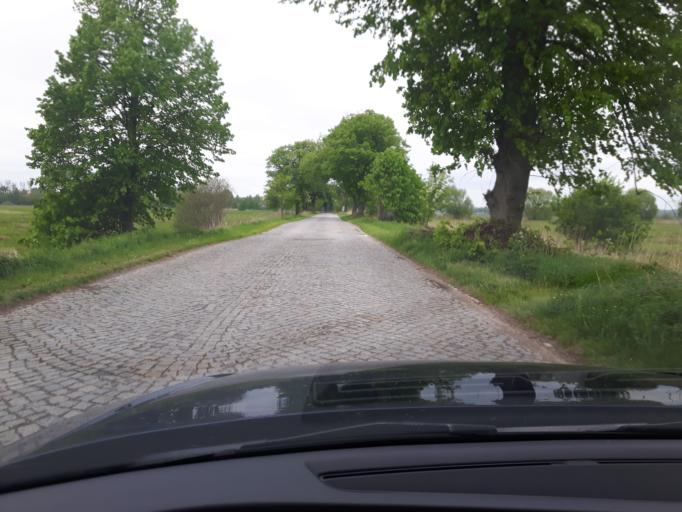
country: DE
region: Mecklenburg-Vorpommern
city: Bad Sulze
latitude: 54.1034
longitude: 12.6740
